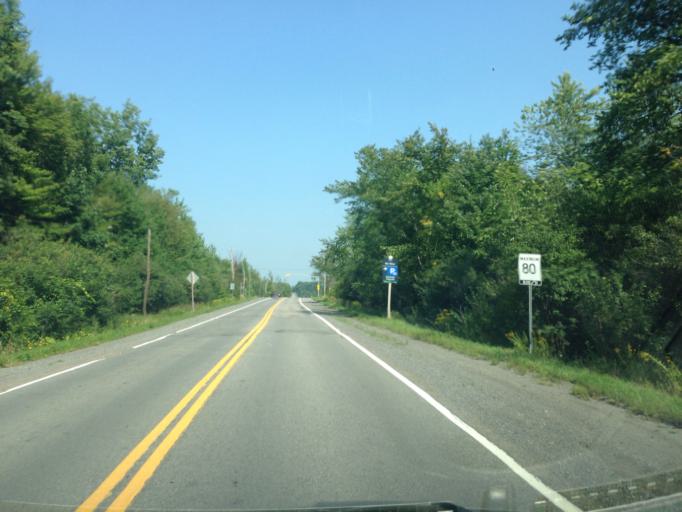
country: CA
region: Ontario
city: Ottawa
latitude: 45.3911
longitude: -75.5511
